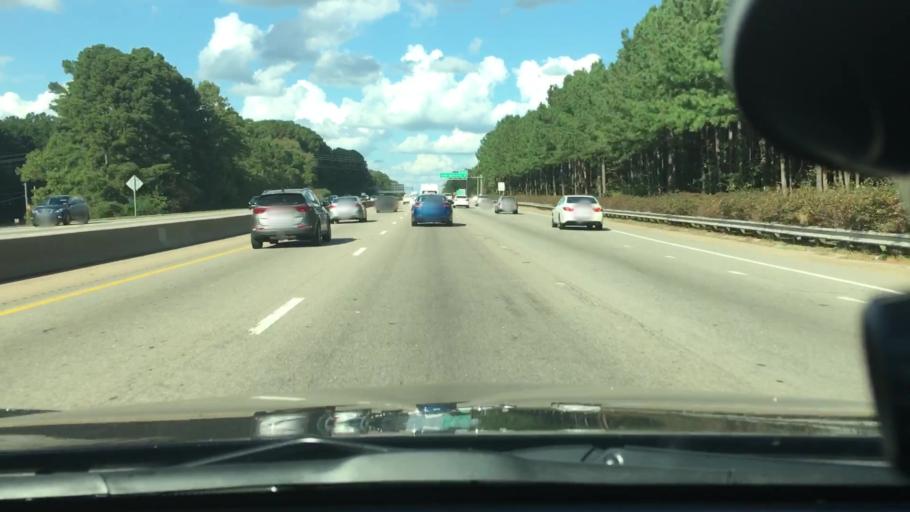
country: US
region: North Carolina
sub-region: Wake County
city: West Raleigh
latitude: 35.8138
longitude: -78.6917
